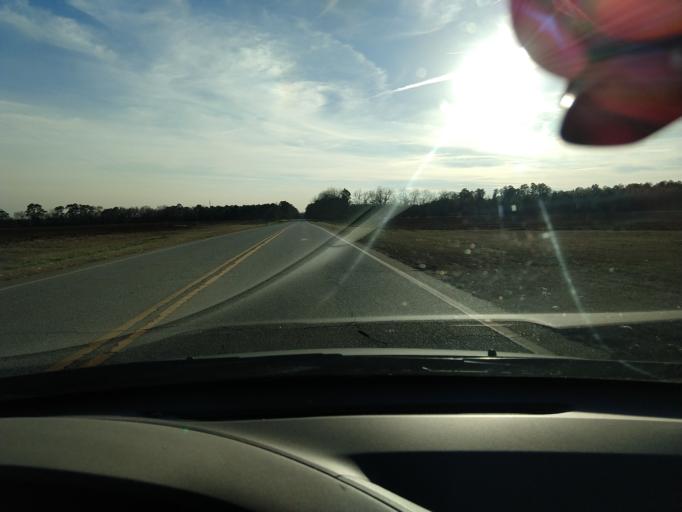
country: US
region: Georgia
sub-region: Sumter County
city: Americus
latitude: 32.1355
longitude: -84.1469
